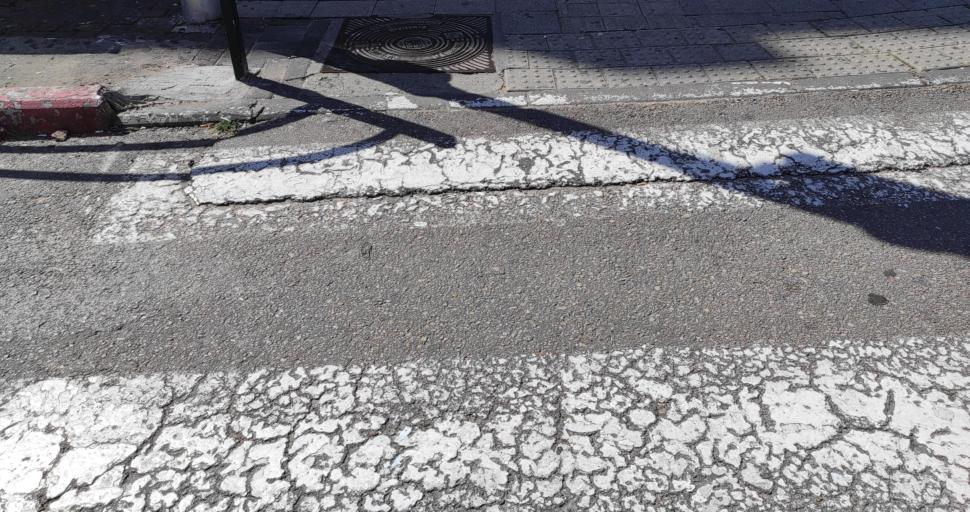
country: IL
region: Central District
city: Netanya
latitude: 32.3281
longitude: 34.8582
